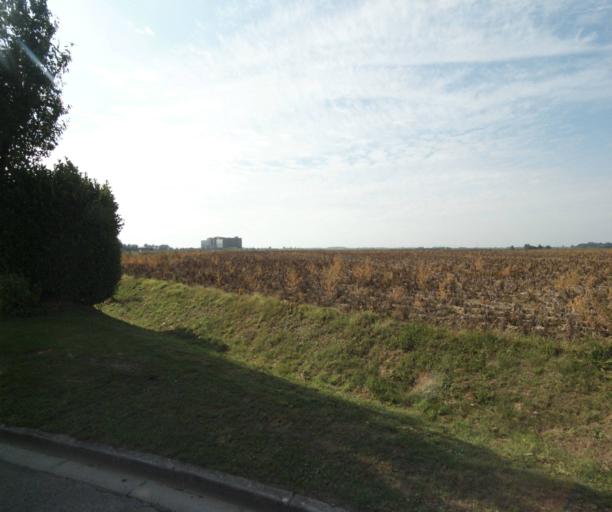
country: FR
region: Nord-Pas-de-Calais
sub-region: Departement du Nord
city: Wattignies
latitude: 50.5737
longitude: 3.0269
